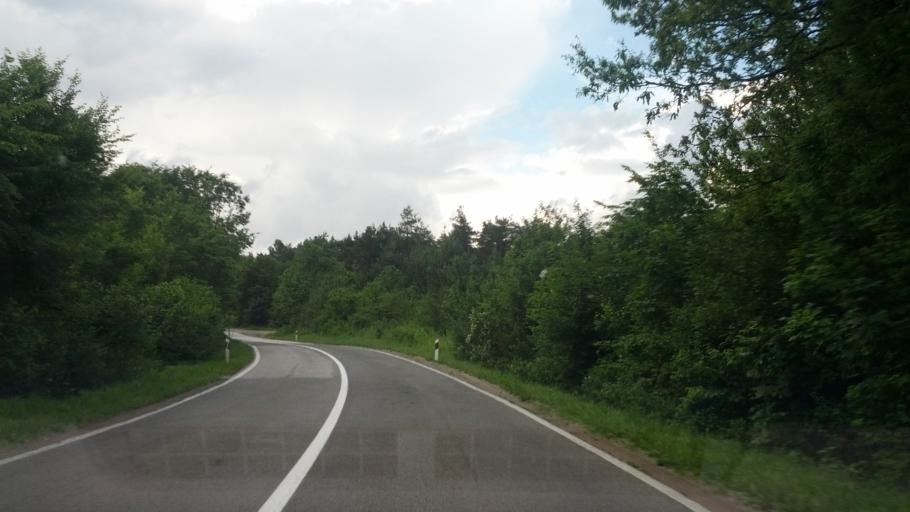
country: HR
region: Licko-Senjska
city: Jezerce
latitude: 44.9284
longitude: 15.7021
